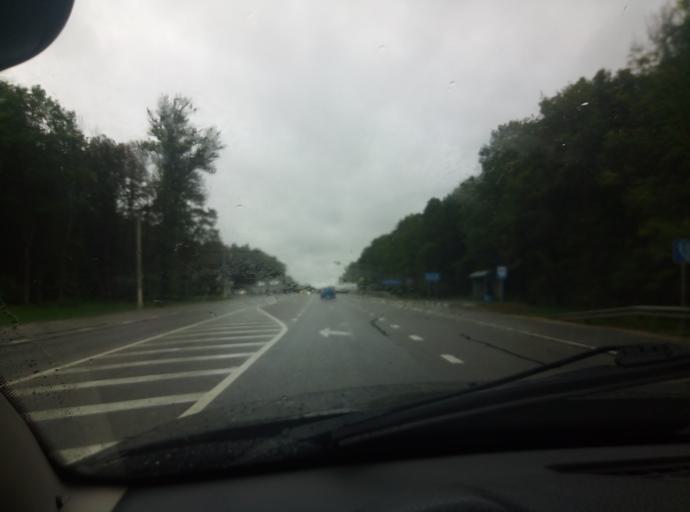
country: RU
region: Tula
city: Leninskiy
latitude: 54.3950
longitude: 37.5064
